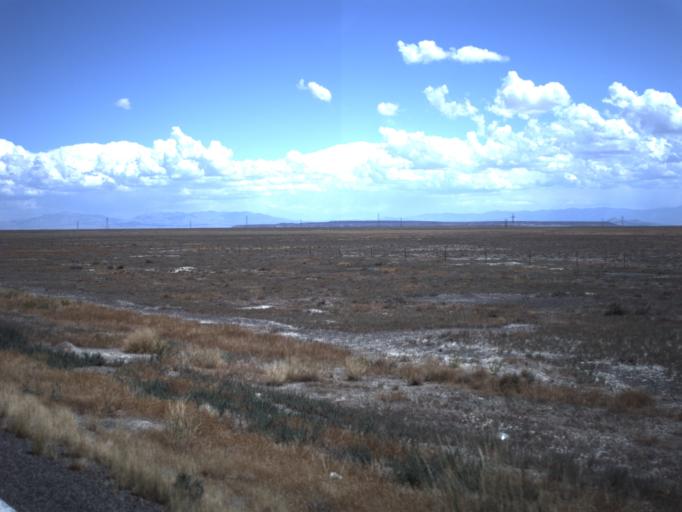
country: US
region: Utah
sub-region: Millard County
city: Delta
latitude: 39.2250
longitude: -112.9409
